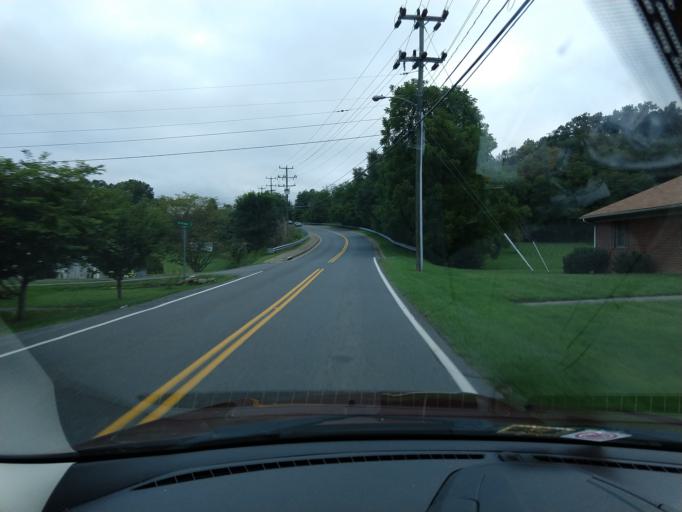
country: US
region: Virginia
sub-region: City of Covington
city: Fairlawn
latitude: 37.7602
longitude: -79.9883
